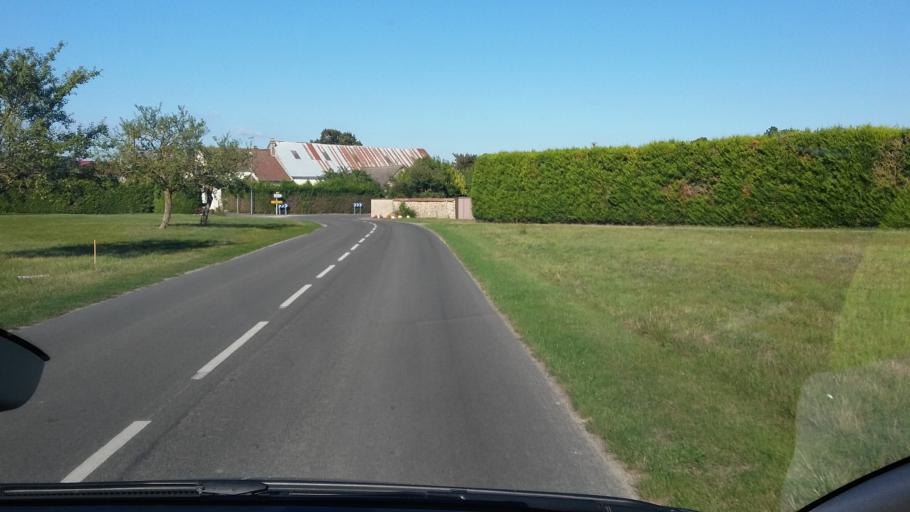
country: FR
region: Champagne-Ardenne
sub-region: Departement de la Marne
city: Fere-Champenoise
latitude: 48.8275
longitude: 3.9309
